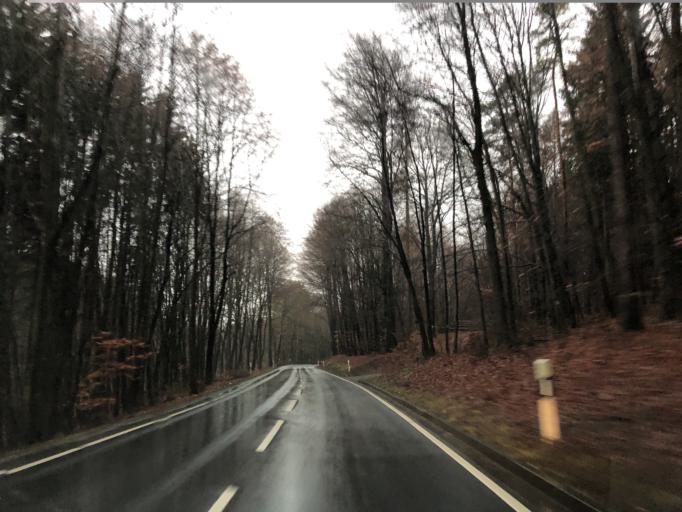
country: DE
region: Hesse
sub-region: Regierungsbezirk Darmstadt
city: Bad Konig
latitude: 49.7326
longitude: 9.0478
